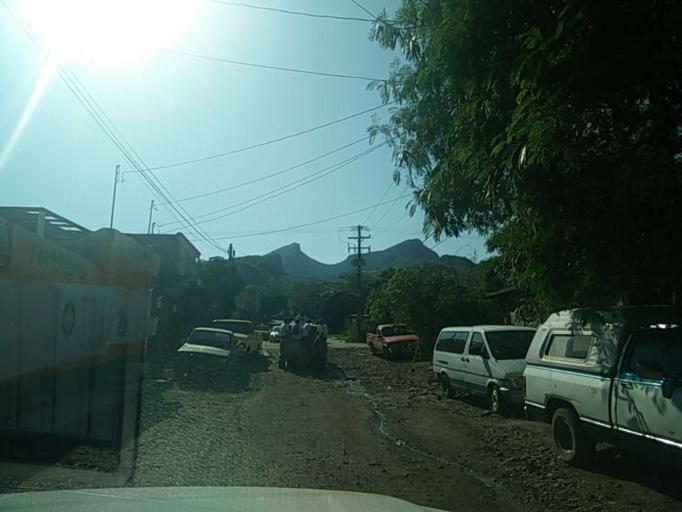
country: MX
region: Sonora
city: Heroica Guaymas
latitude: 27.9371
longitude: -110.8823
